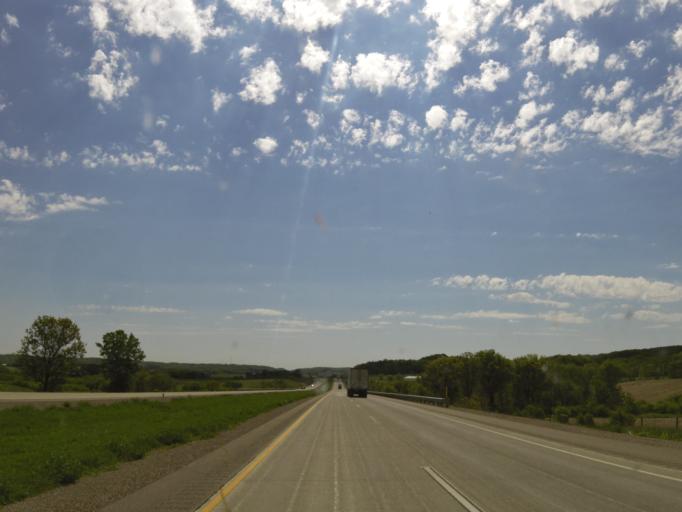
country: US
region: Wisconsin
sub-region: Trempealeau County
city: Osseo
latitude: 44.6301
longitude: -91.2871
